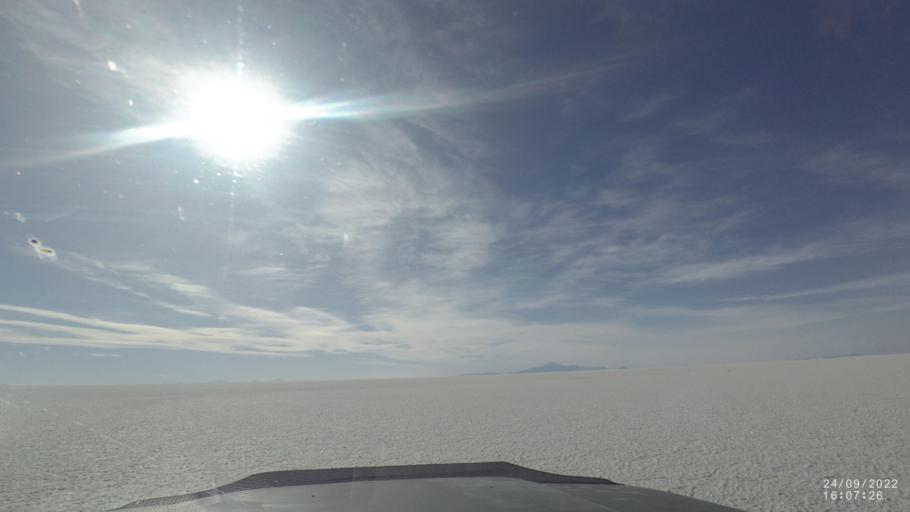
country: BO
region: Potosi
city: Colchani
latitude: -20.2996
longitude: -67.3024
